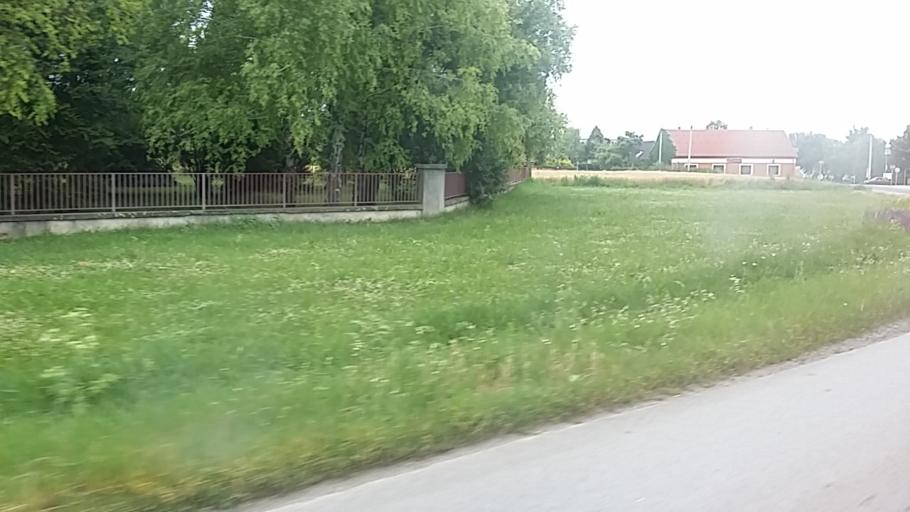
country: HU
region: Baranya
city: Boly
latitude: 45.9854
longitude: 18.5347
